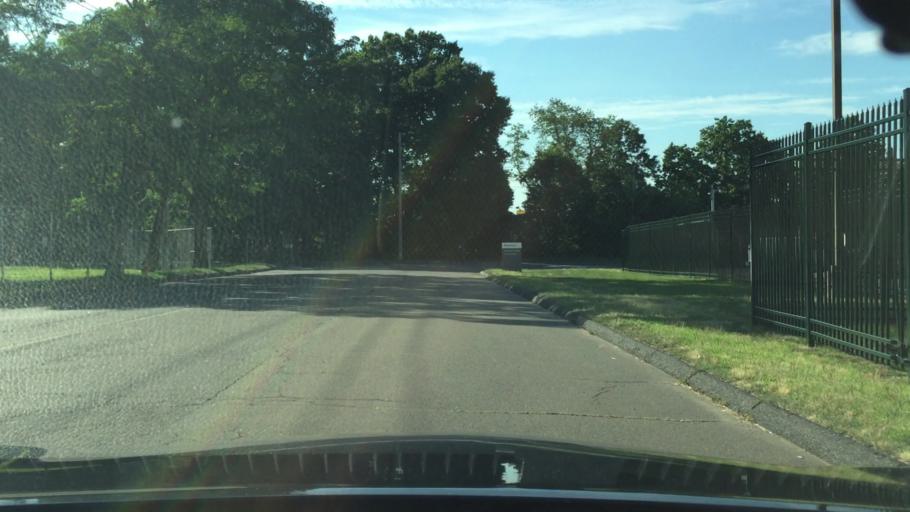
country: US
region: Connecticut
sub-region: New Haven County
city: North Haven
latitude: 41.3379
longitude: -72.8715
